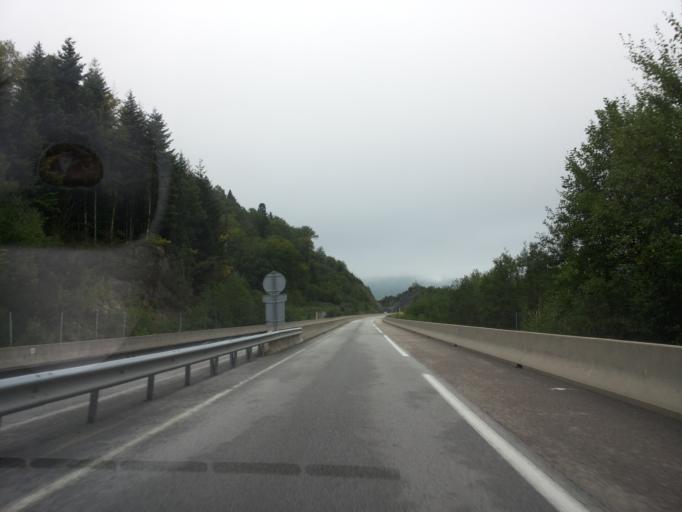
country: FR
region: Lorraine
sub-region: Departement des Vosges
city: Rupt-sur-Moselle
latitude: 47.9306
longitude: 6.6483
